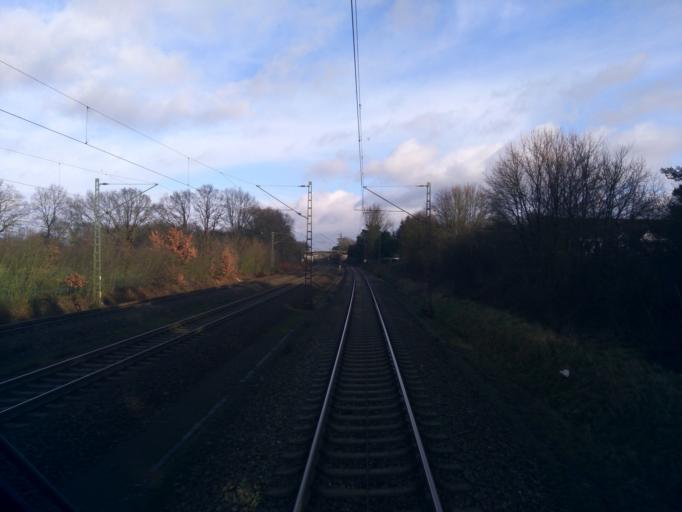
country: DE
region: Lower Saxony
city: Rotenburg
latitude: 53.1172
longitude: 9.4085
